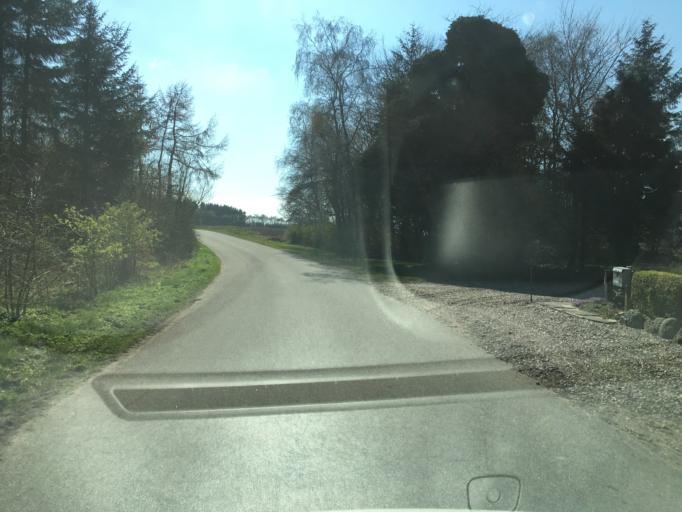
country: DK
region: South Denmark
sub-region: Aabenraa Kommune
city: Krusa
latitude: 54.9254
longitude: 9.4785
